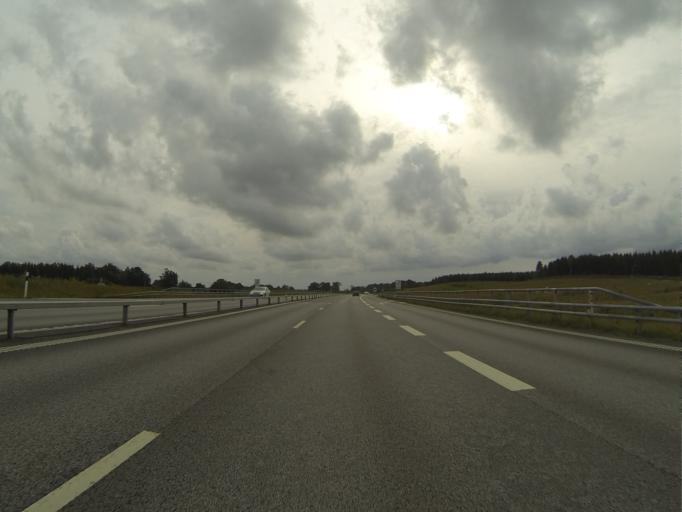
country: SE
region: Skane
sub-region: Horby Kommun
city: Hoerby
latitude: 55.8668
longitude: 13.6950
